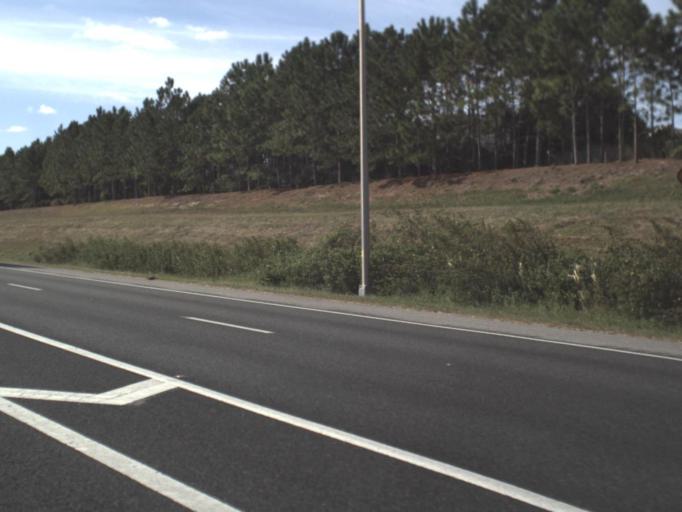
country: US
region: Florida
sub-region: Orange County
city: Gotha
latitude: 28.5390
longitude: -81.5237
